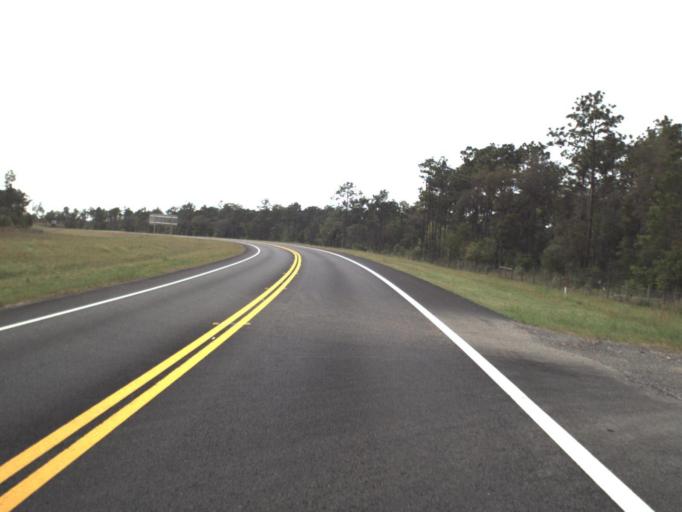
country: US
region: Florida
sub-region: Okaloosa County
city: Niceville
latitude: 30.5332
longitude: -86.4210
